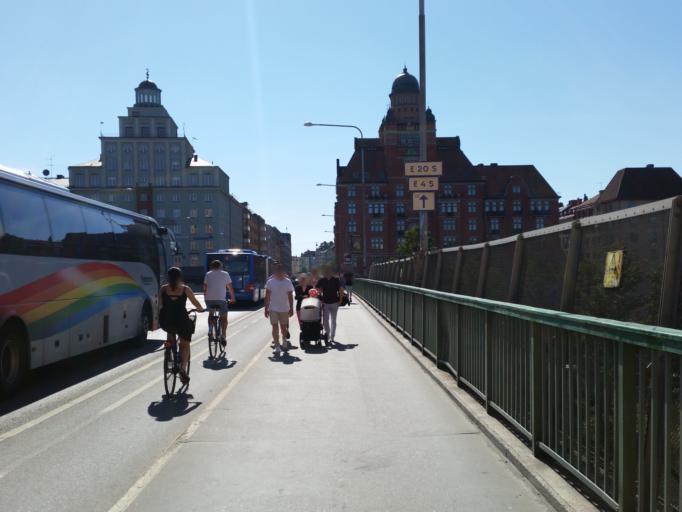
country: SE
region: Stockholm
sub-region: Stockholms Kommun
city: Stockholm
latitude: 59.3379
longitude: 18.0351
